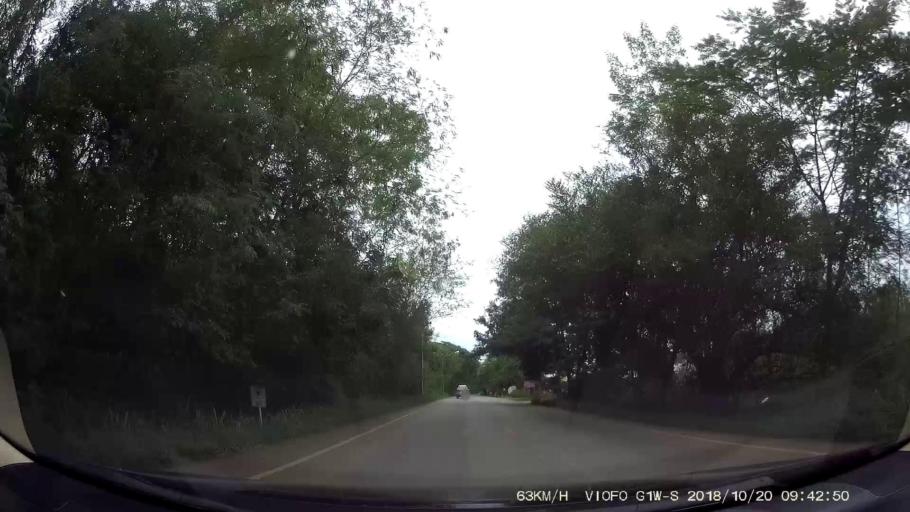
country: TH
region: Chaiyaphum
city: Khon San
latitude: 16.4677
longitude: 101.9507
